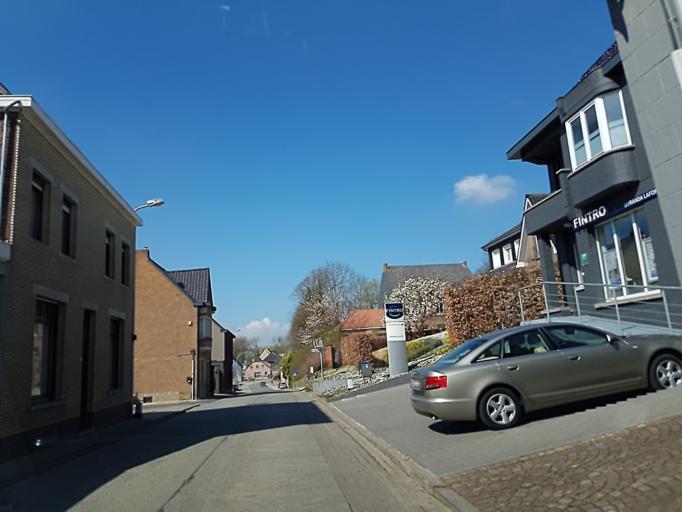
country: BE
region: Flanders
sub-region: Provincie Oost-Vlaanderen
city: Sint-Maria-Lierde
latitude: 50.8218
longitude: 3.8461
